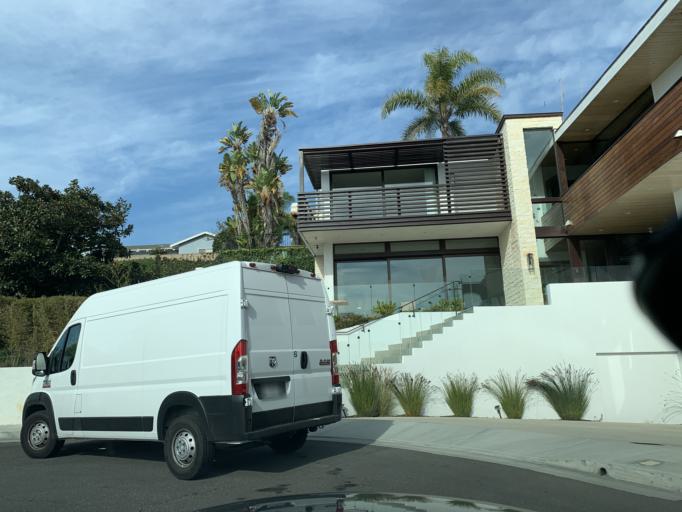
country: US
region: California
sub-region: Los Angeles County
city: Hermosa Beach
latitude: 33.8786
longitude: -118.3878
